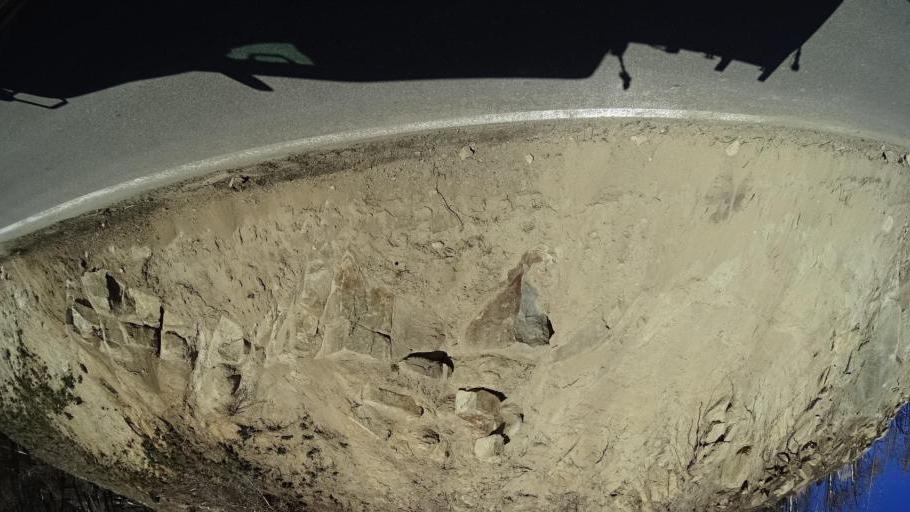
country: US
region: California
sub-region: Kern County
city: Alta Sierra
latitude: 35.7475
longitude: -118.5567
